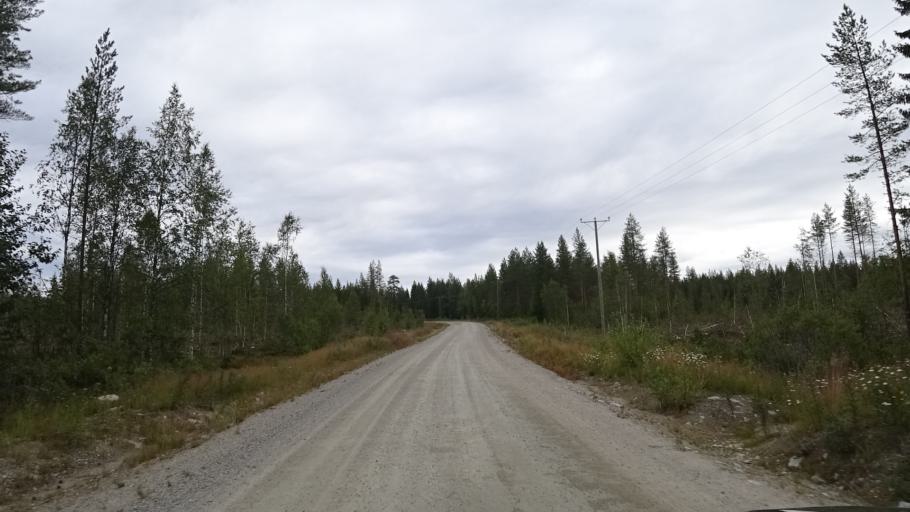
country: FI
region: North Karelia
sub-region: Joensuu
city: Eno
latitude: 63.1689
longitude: 30.5638
